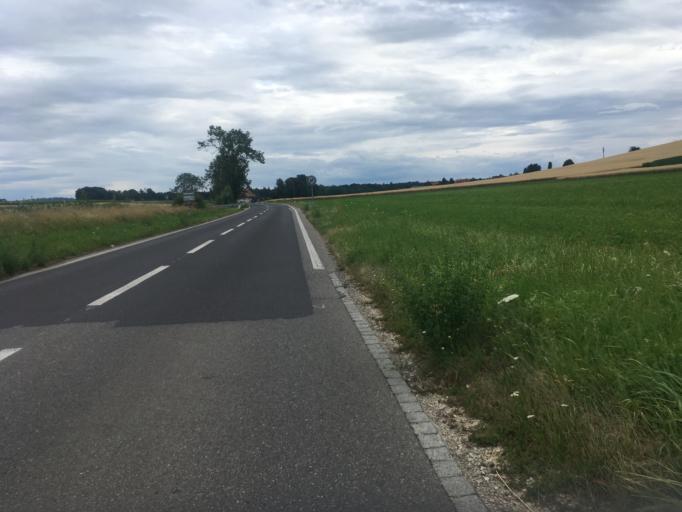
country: CH
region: Bern
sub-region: Seeland District
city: Erlach
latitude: 47.0373
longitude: 7.0953
